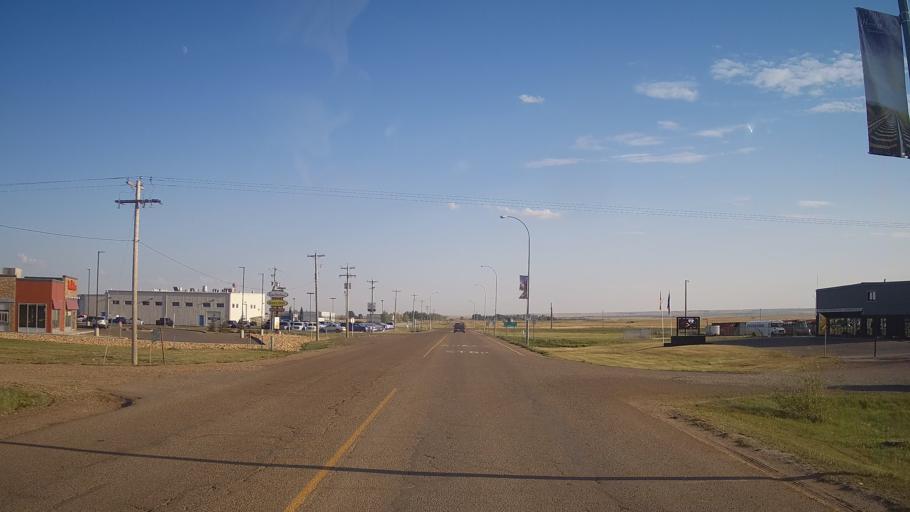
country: CA
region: Alberta
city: Hanna
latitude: 51.6369
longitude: -111.9419
